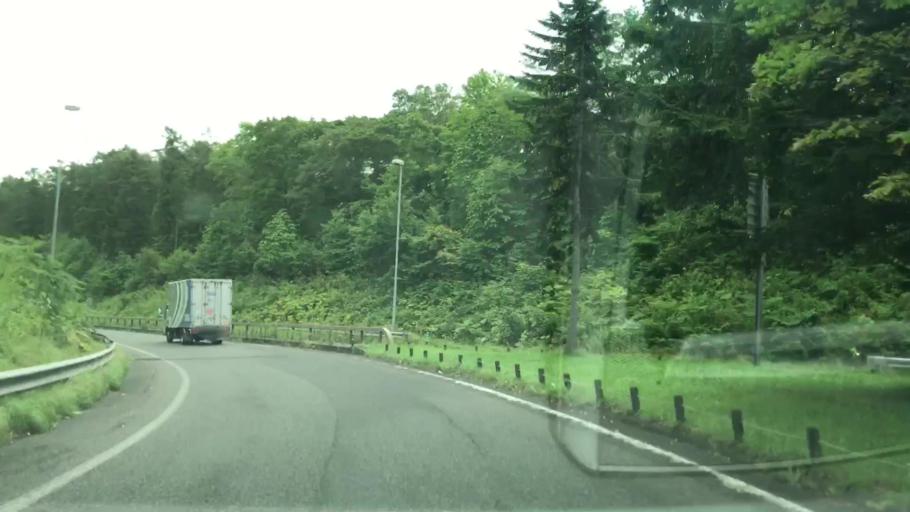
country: JP
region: Hokkaido
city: Chitose
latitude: 42.8113
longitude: 141.6265
